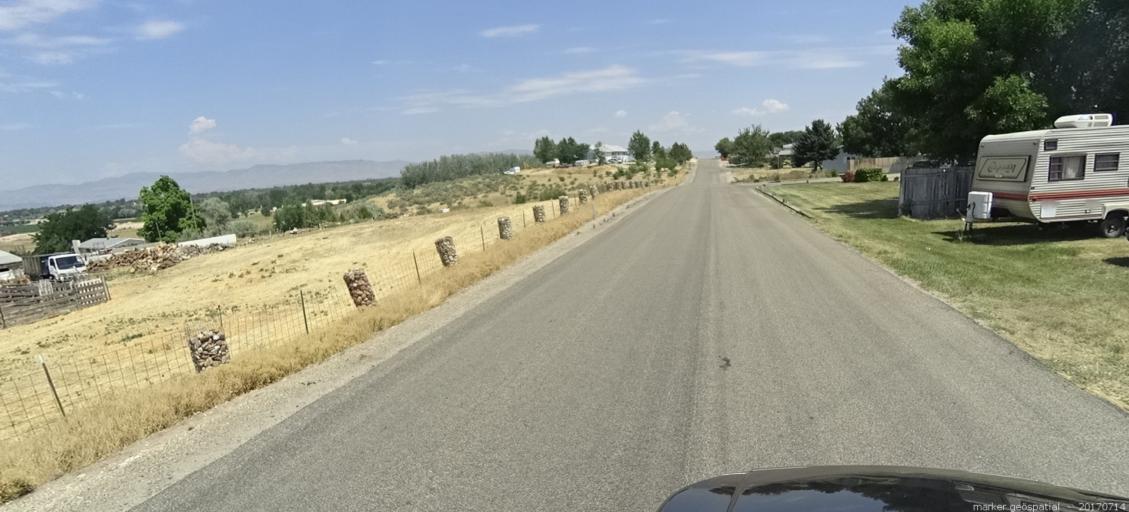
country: US
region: Idaho
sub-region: Ada County
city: Meridian
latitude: 43.5355
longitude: -116.3207
